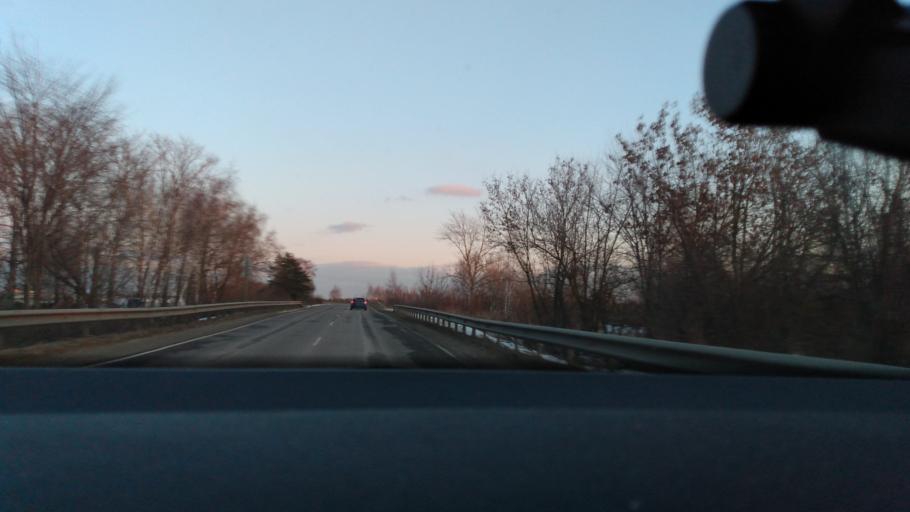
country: RU
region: Moskovskaya
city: Kolomna
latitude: 55.0875
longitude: 38.9192
